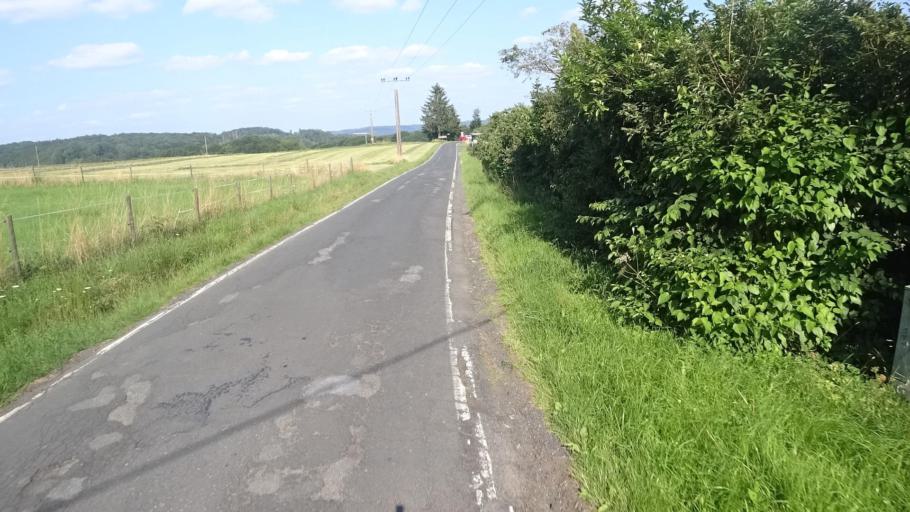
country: DE
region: Rheinland-Pfalz
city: Sankt Katharinen
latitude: 50.5616
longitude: 7.3518
